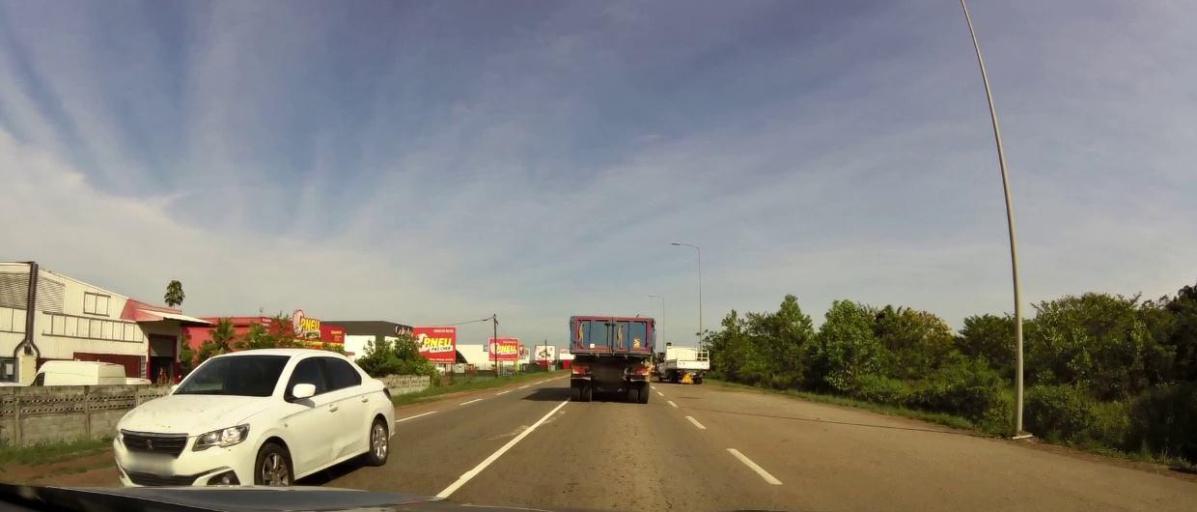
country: GF
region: Guyane
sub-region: Guyane
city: Cayenne
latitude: 4.9046
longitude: -52.3183
